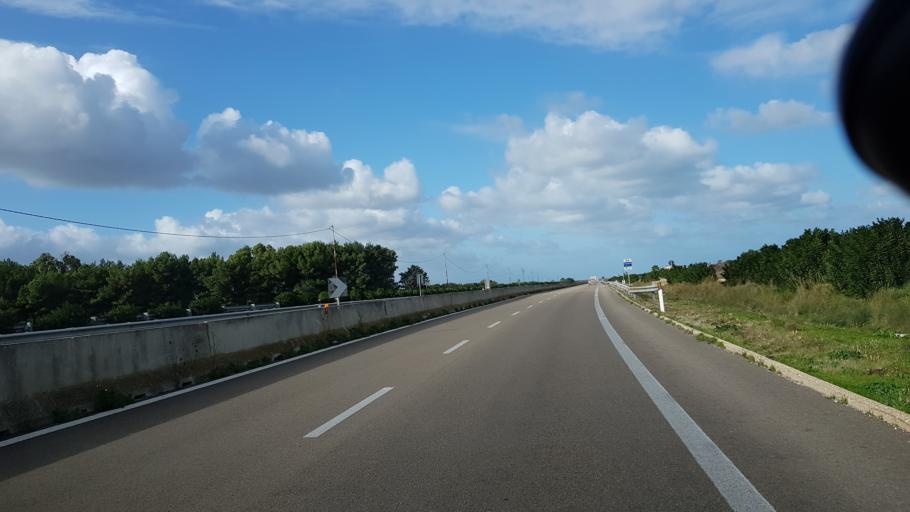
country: IT
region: Apulia
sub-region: Provincia di Brindisi
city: San Vito dei Normanni
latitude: 40.7210
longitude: 17.7503
